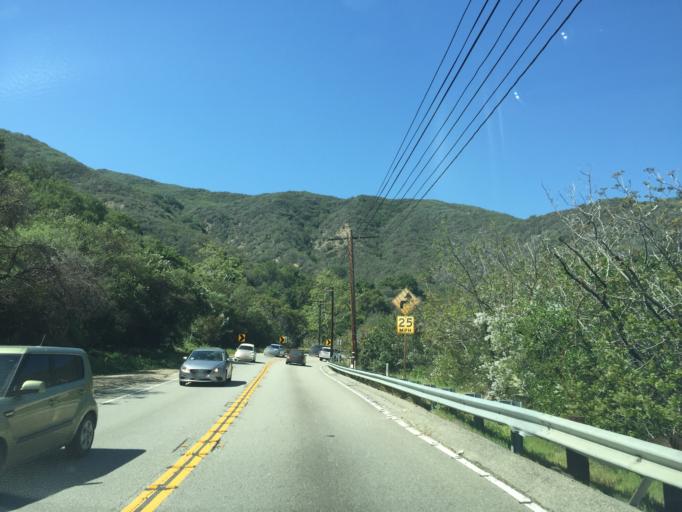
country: US
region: California
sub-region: Los Angeles County
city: Topanga
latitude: 34.0749
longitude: -118.5896
